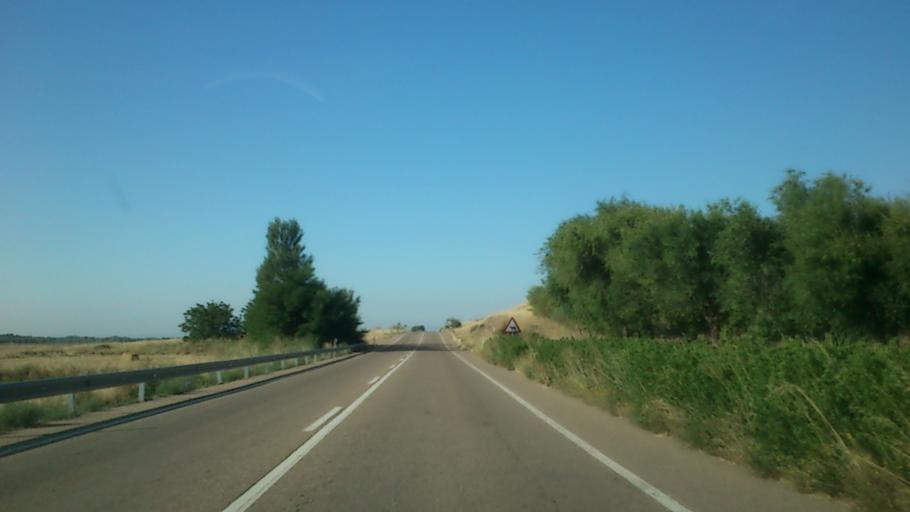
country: ES
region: Aragon
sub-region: Provincia de Zaragoza
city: San Mateo de Gallego
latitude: 41.8112
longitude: -0.8062
